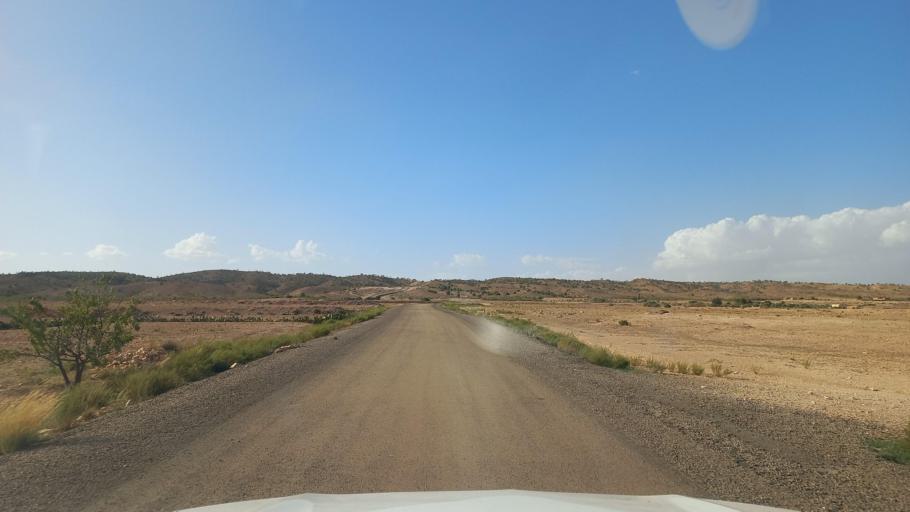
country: TN
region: Al Qasrayn
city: Sbiba
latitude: 35.3500
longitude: 8.9878
